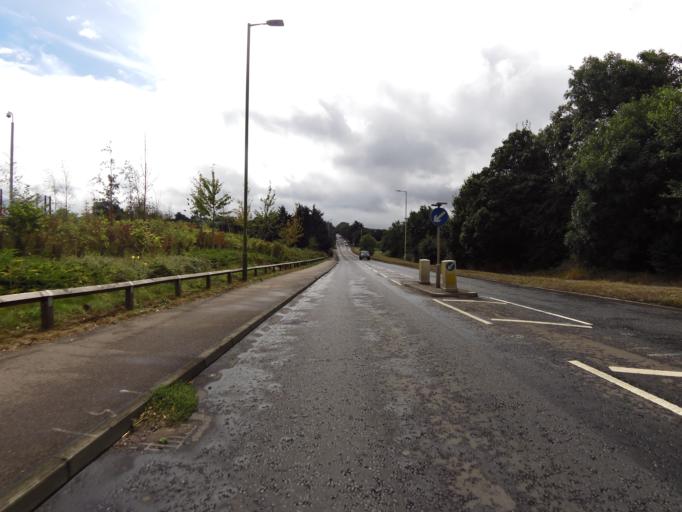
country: GB
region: England
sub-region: Hertfordshire
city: Radlett
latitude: 51.7040
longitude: -0.3282
